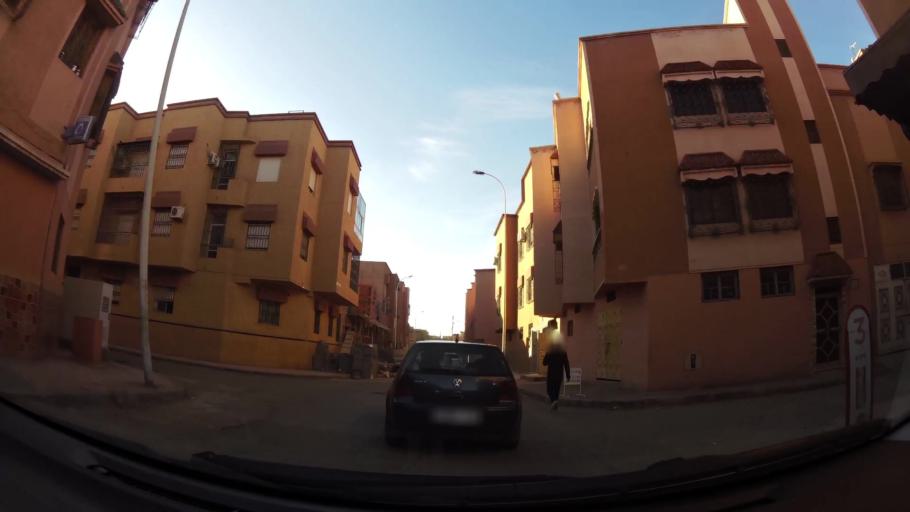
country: MA
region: Marrakech-Tensift-Al Haouz
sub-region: Marrakech
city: Marrakesh
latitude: 31.6179
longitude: -8.0596
